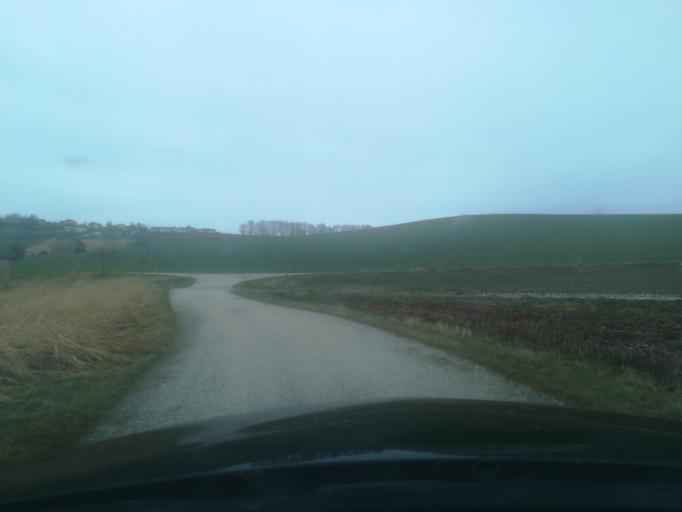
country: AT
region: Upper Austria
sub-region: Wels-Land
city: Neukirchen bei Lambach
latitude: 48.1019
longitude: 13.8213
